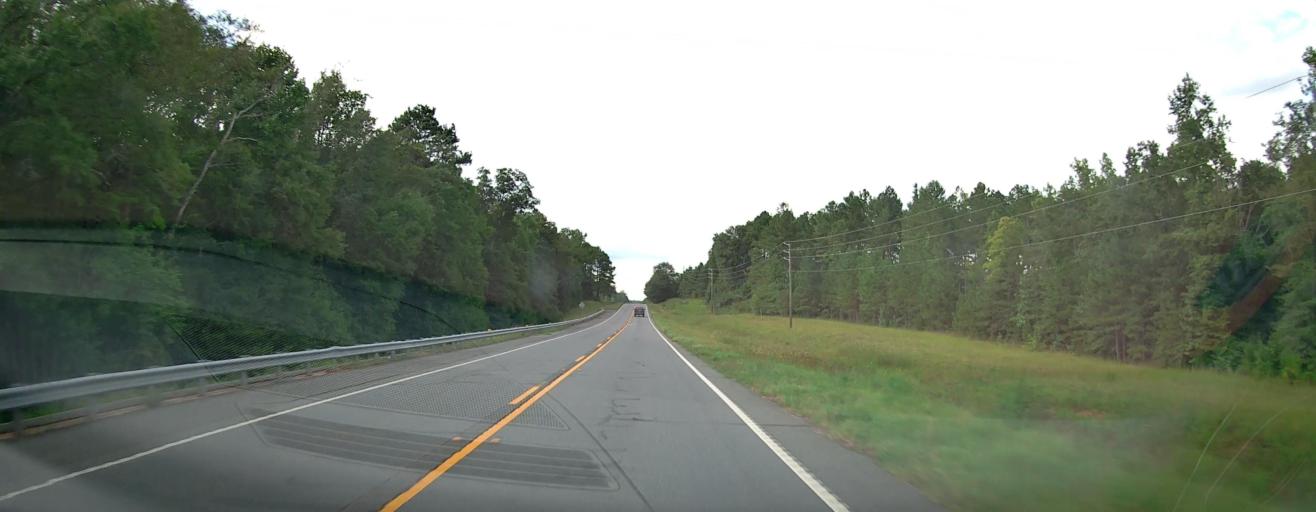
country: US
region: Georgia
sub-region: Meriwether County
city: Greenville
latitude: 33.0463
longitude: -84.5670
